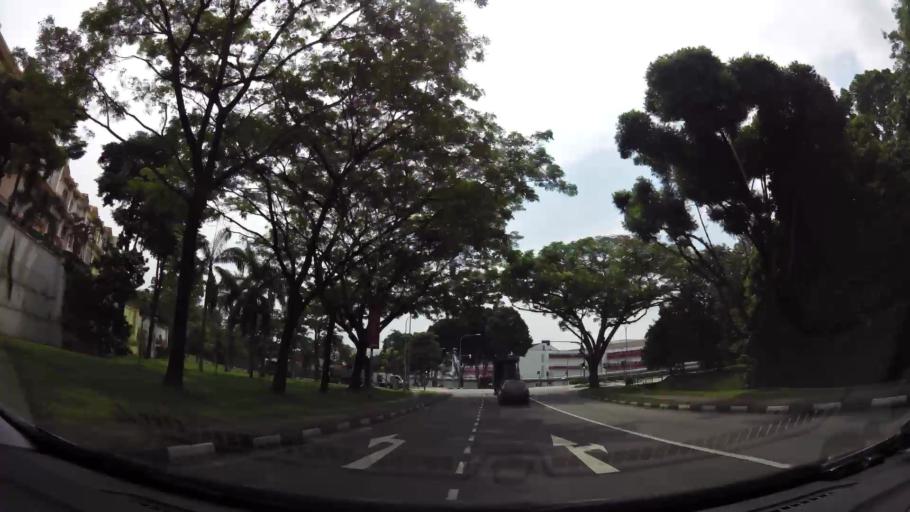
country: SG
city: Singapore
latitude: 1.3622
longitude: 103.9714
